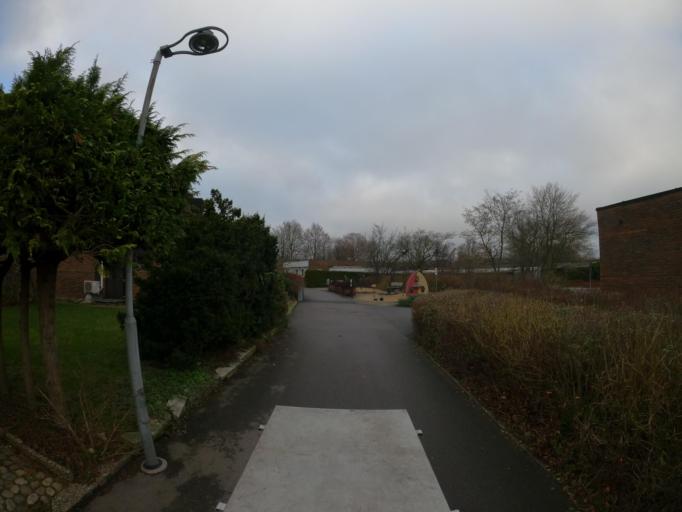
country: SE
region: Skane
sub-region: Svedala Kommun
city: Svedala
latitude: 55.5215
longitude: 13.2112
